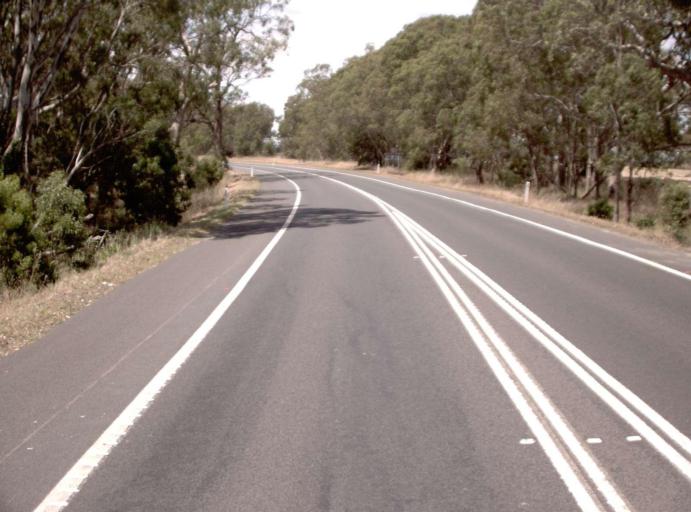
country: AU
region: Victoria
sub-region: Latrobe
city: Traralgon
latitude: -38.1680
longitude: 146.6963
